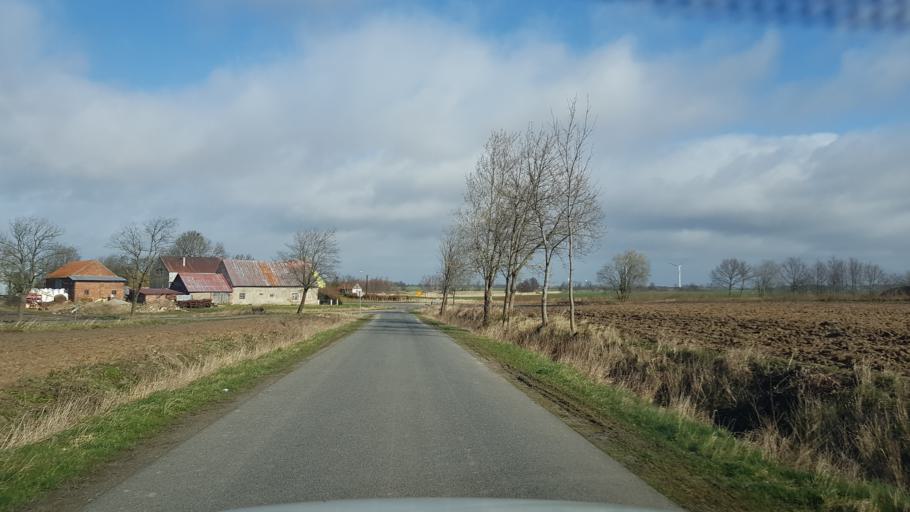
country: PL
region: West Pomeranian Voivodeship
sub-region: Powiat slawienski
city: Slawno
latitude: 54.5083
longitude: 16.6536
